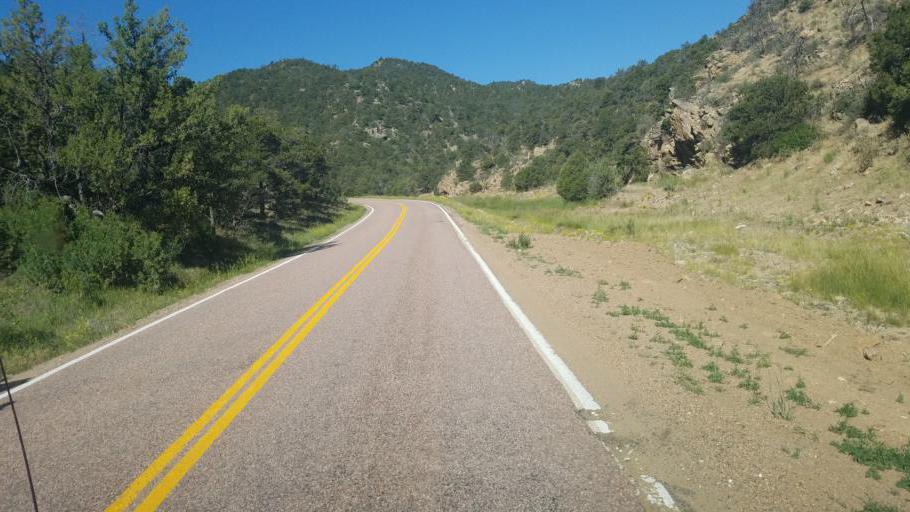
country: US
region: Colorado
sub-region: Fremont County
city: Canon City
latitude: 38.4253
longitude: -105.4037
